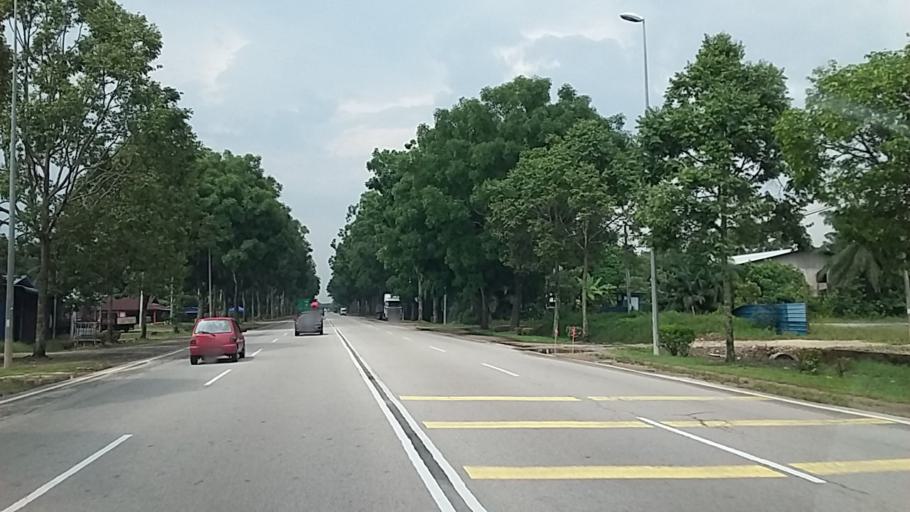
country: MY
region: Johor
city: Parit Raja
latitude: 1.8712
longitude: 103.1298
